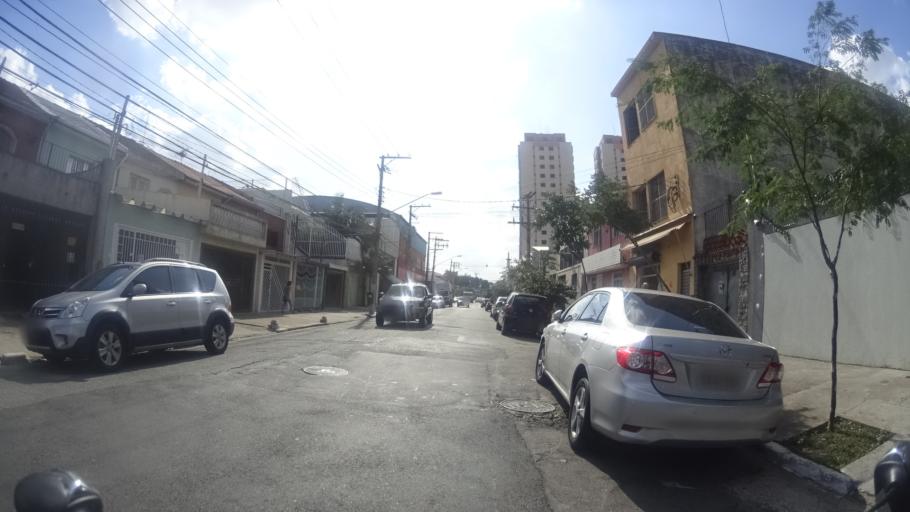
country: BR
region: Sao Paulo
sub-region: Sao Paulo
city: Sao Paulo
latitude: -23.5492
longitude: -46.6085
